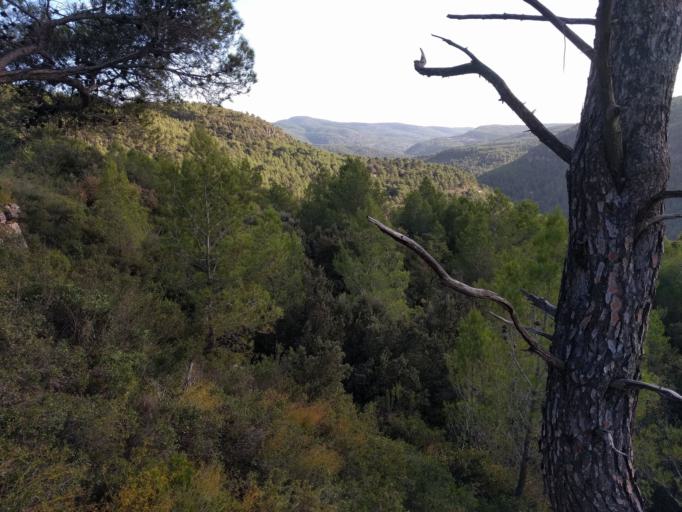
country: ES
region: Catalonia
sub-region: Provincia de Tarragona
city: Querol
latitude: 41.4583
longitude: 1.4021
